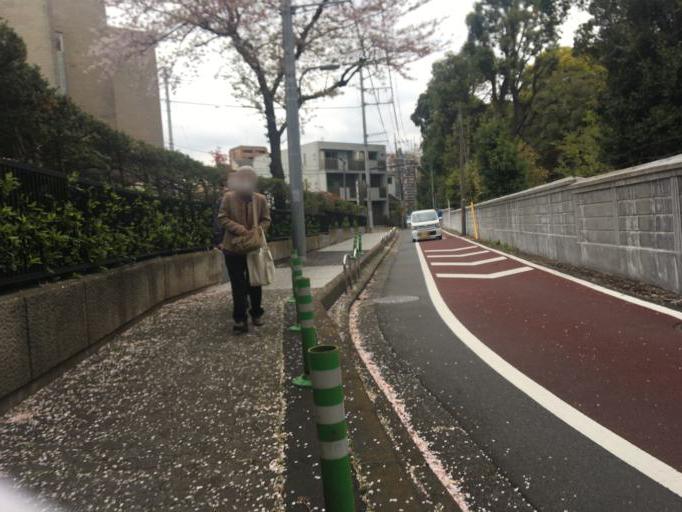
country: JP
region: Tokyo
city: Tokyo
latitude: 35.6956
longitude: 139.6517
